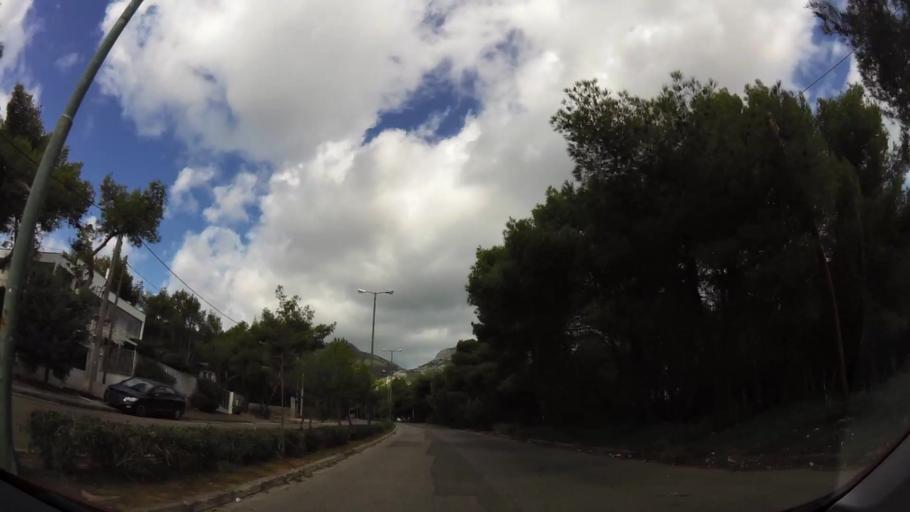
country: GR
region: Attica
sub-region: Nomarchia Anatolikis Attikis
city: Thrakomakedones
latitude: 38.1328
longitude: 23.7630
